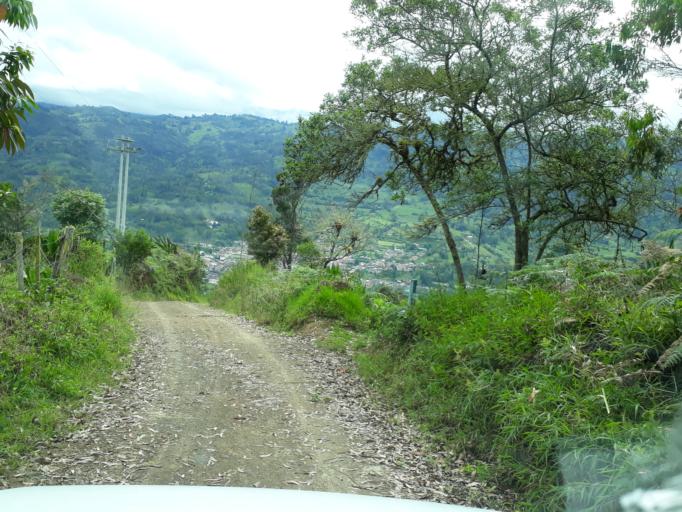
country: CO
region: Cundinamarca
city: Junin
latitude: 4.8028
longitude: -73.6476
